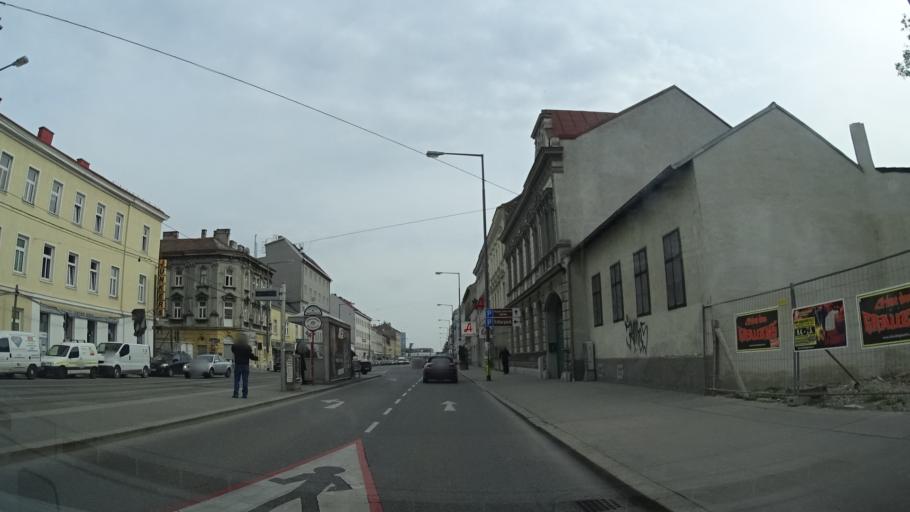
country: AT
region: Lower Austria
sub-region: Politischer Bezirk Korneuburg
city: Langenzersdorf
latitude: 48.2688
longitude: 16.3919
